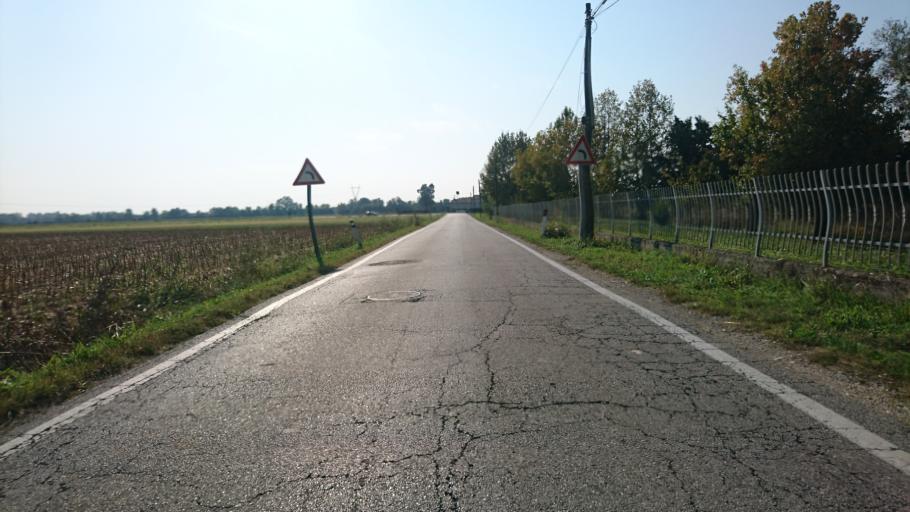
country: IT
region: Veneto
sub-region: Provincia di Padova
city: Gazzo
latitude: 45.5969
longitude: 11.6928
